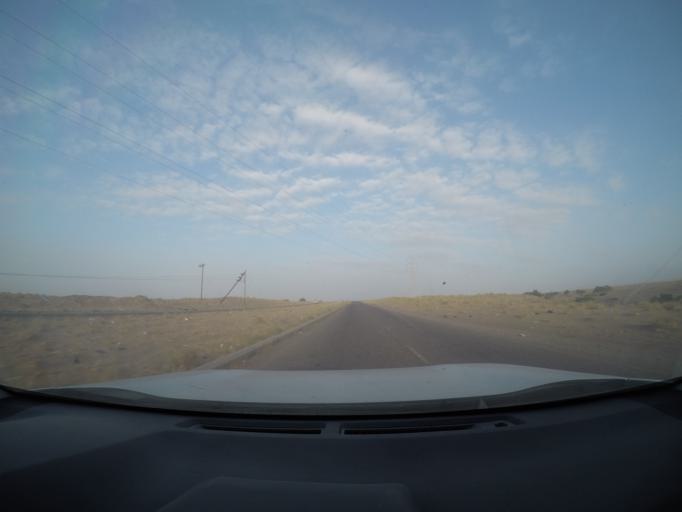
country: YE
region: Lahij
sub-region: Al  Hawtah
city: Lahij
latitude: 13.1469
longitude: 44.8385
